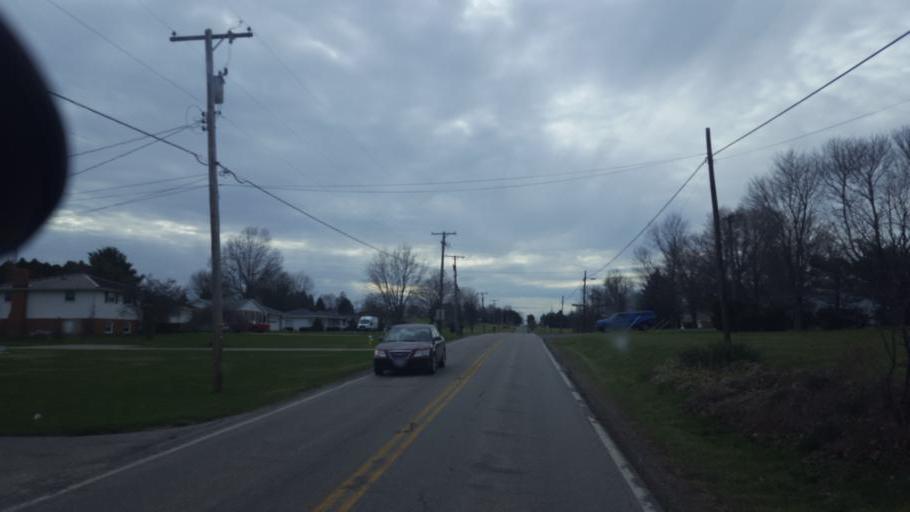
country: US
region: Ohio
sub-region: Richland County
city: Lexington
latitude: 40.6960
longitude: -82.5277
